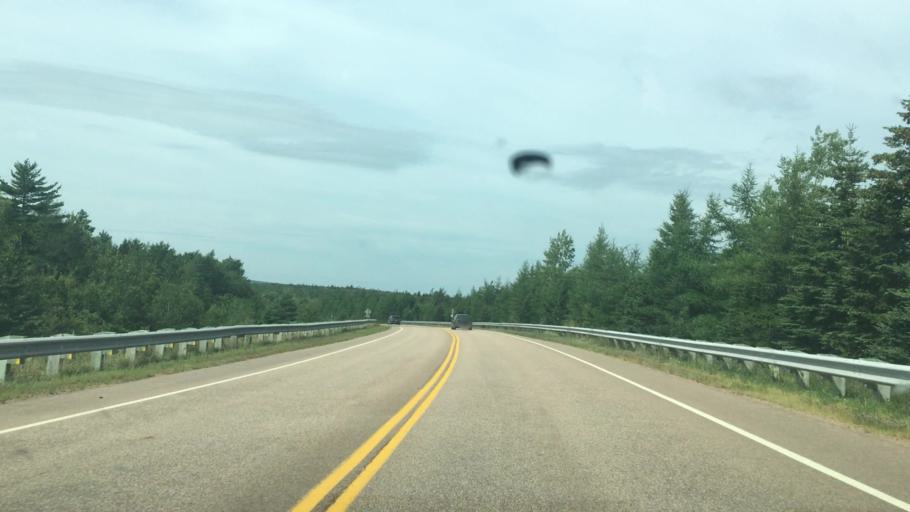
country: CA
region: Nova Scotia
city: Port Hawkesbury
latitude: 45.6050
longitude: -61.2979
